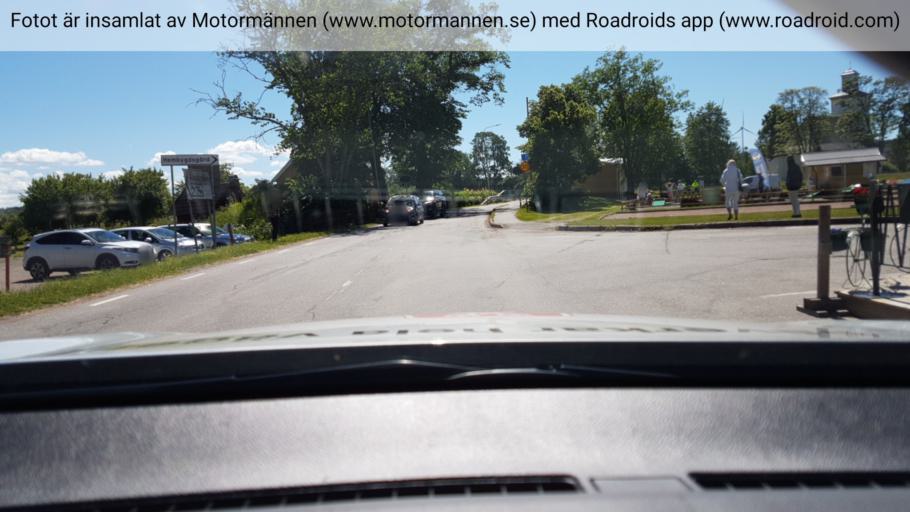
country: SE
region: Vaestra Goetaland
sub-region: Toreboda Kommun
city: Toereboda
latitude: 58.8021
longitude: 14.0597
